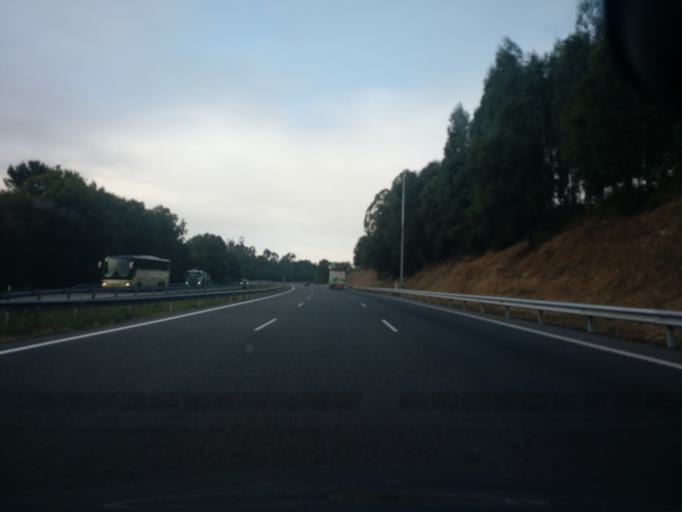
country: ES
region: Galicia
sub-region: Provincia da Coruna
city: Abegondo
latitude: 43.1849
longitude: -8.3114
